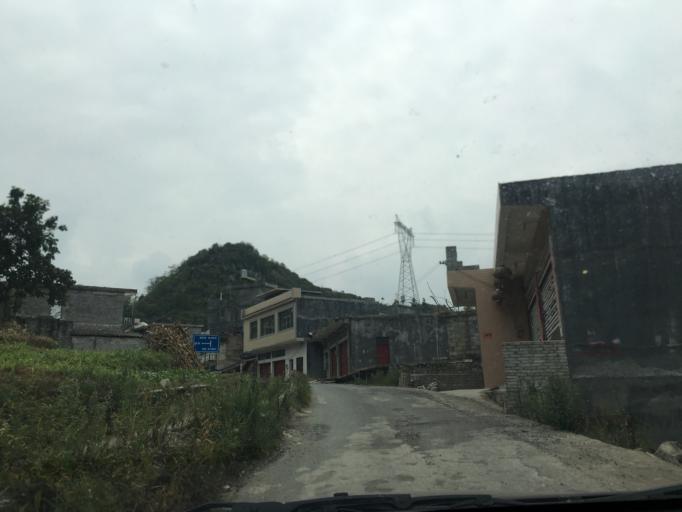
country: CN
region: Guangxi Zhuangzu Zizhiqu
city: Xinzhou
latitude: 25.5387
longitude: 105.5898
